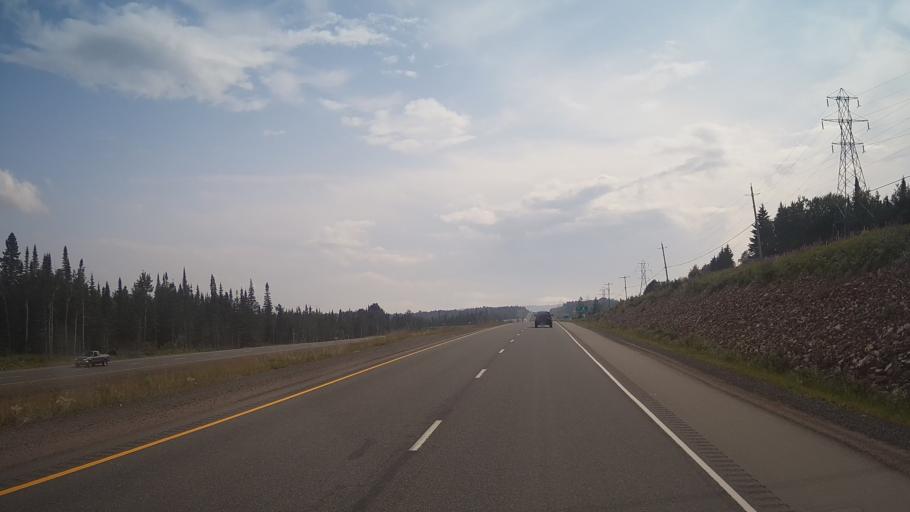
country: CA
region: Ontario
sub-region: Thunder Bay District
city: Thunder Bay
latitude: 48.6089
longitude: -88.7757
